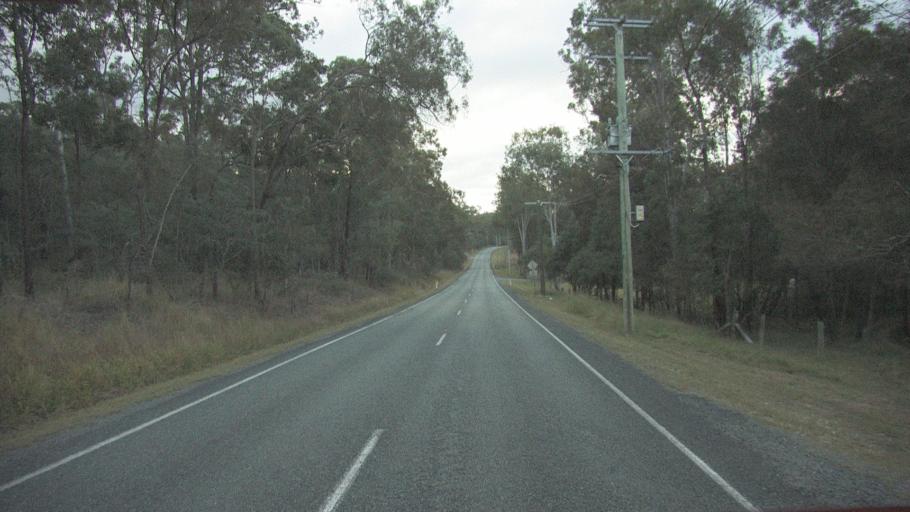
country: AU
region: Queensland
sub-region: Logan
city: Windaroo
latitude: -27.8116
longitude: 153.1566
